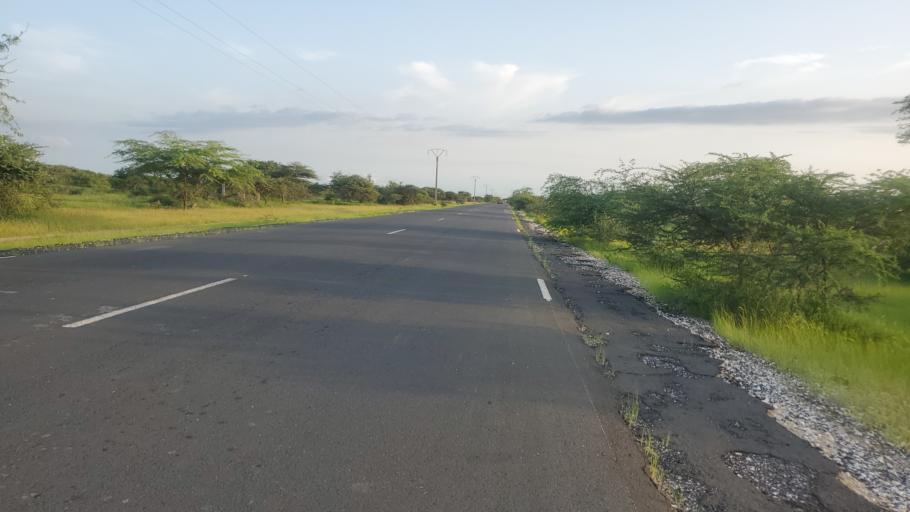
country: SN
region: Saint-Louis
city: Saint-Louis
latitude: 16.1783
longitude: -16.4096
